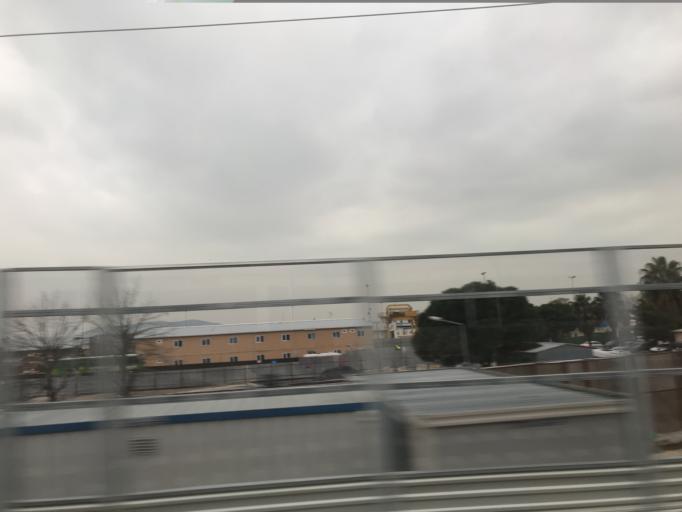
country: TR
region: Istanbul
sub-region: Atasehir
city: Atasehir
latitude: 40.9525
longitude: 29.0980
